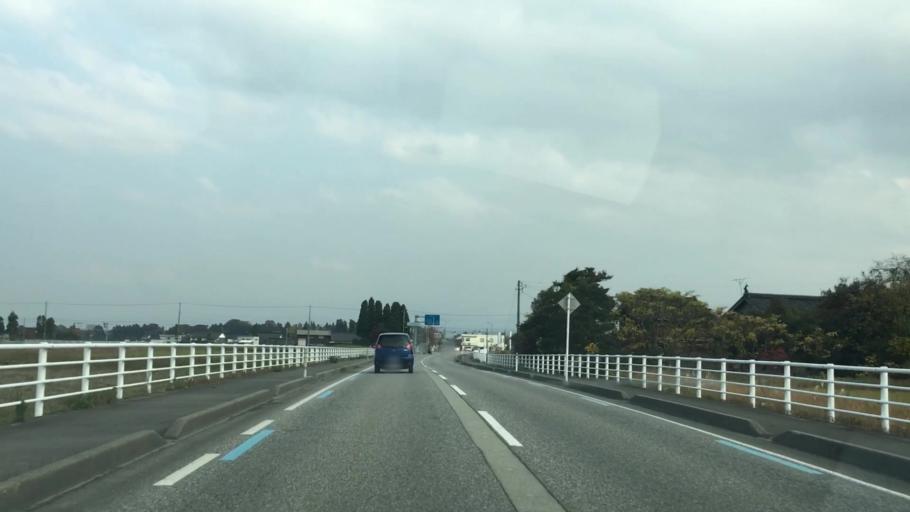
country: JP
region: Toyama
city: Yatsuomachi-higashikumisaka
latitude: 36.6132
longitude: 137.1886
